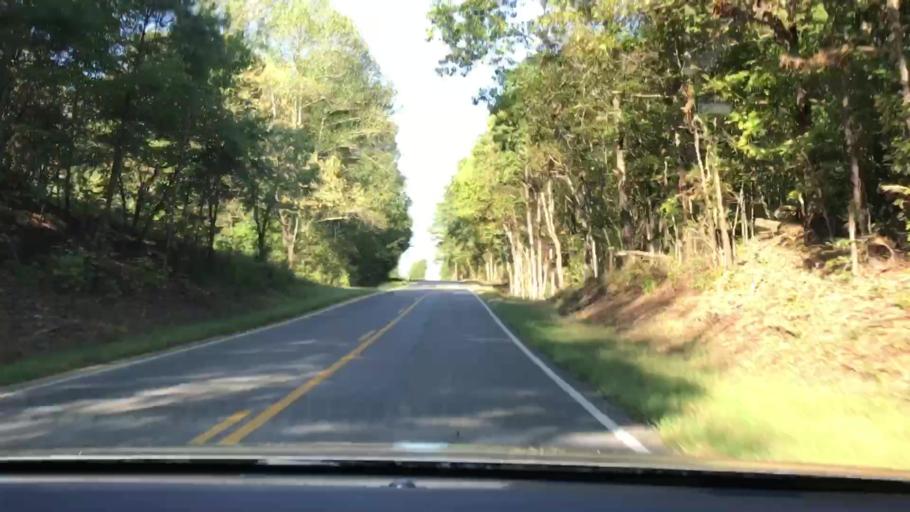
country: US
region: Kentucky
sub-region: Marshall County
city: Benton
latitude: 36.7643
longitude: -88.2101
